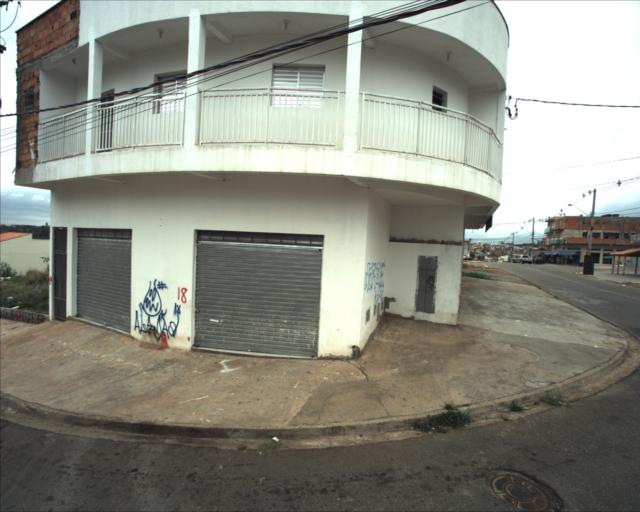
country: BR
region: Sao Paulo
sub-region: Sorocaba
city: Sorocaba
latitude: -23.4317
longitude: -47.5030
